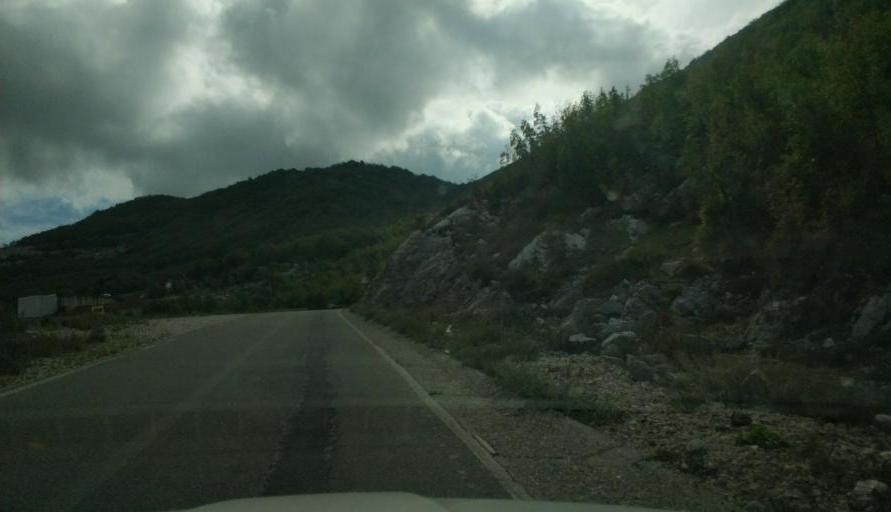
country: AL
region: Durres
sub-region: Rrethi i Krujes
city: Kruje
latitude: 41.5259
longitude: 19.7984
